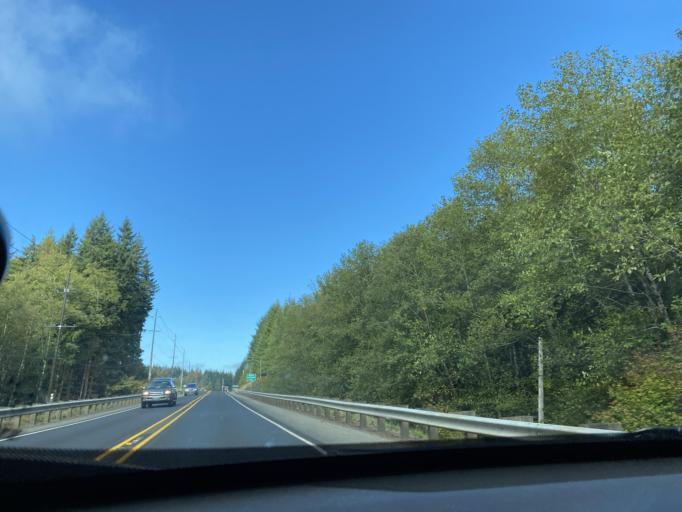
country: US
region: Washington
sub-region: Clallam County
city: Forks
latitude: 47.9605
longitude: -124.3945
